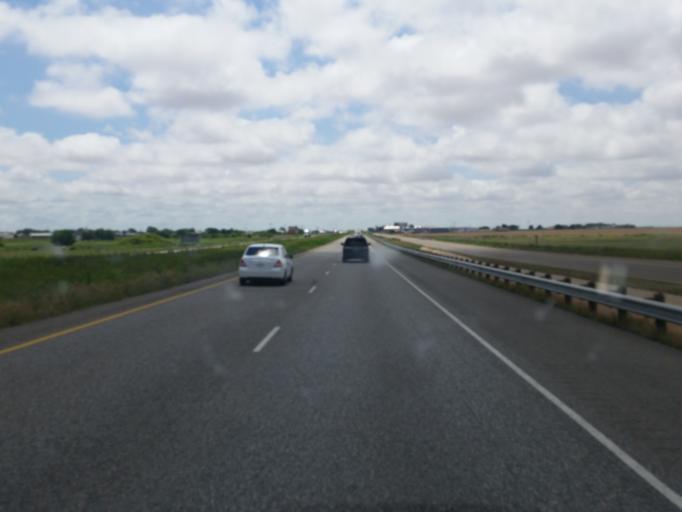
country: US
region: Texas
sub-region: Lubbock County
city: Slaton
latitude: 33.4276
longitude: -101.6563
